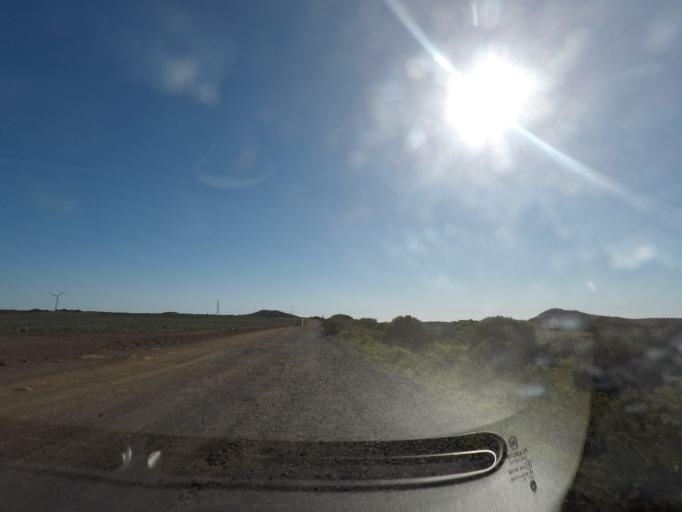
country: PT
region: Madeira
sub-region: Calheta
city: Arco da Calheta
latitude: 32.7576
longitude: -17.1040
